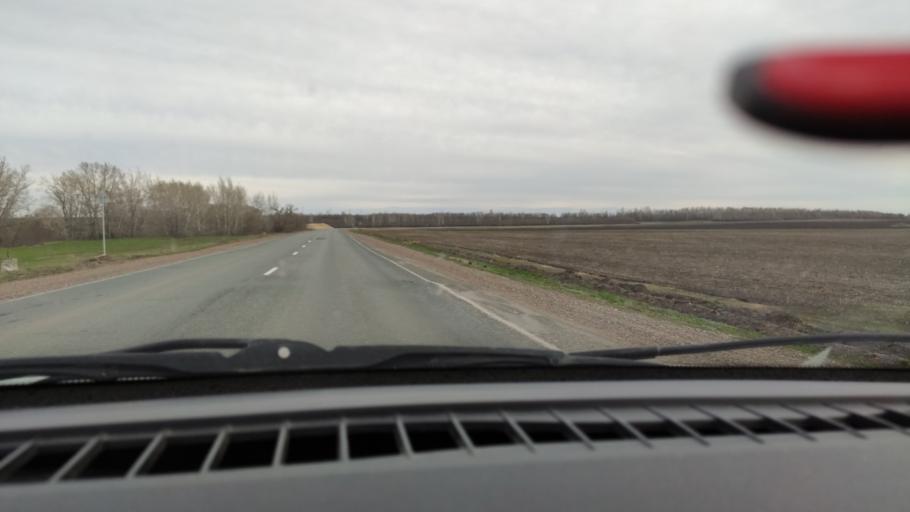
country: RU
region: Bashkortostan
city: Yermolayevo
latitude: 52.4693
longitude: 55.8310
